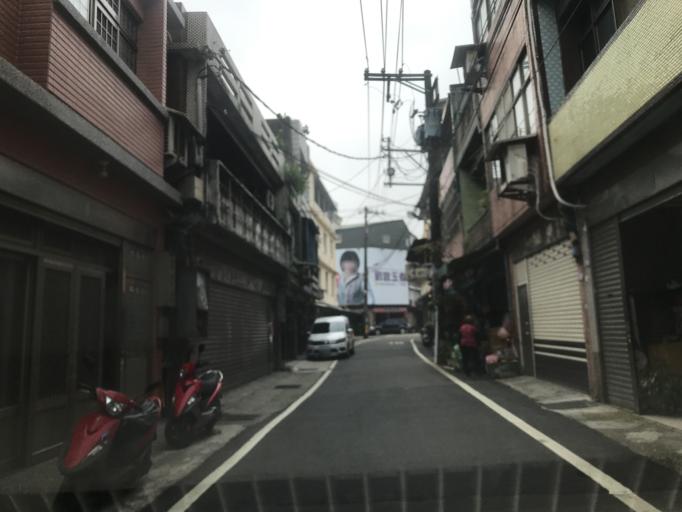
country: TW
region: Taiwan
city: Taoyuan City
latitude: 24.9659
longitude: 121.2293
